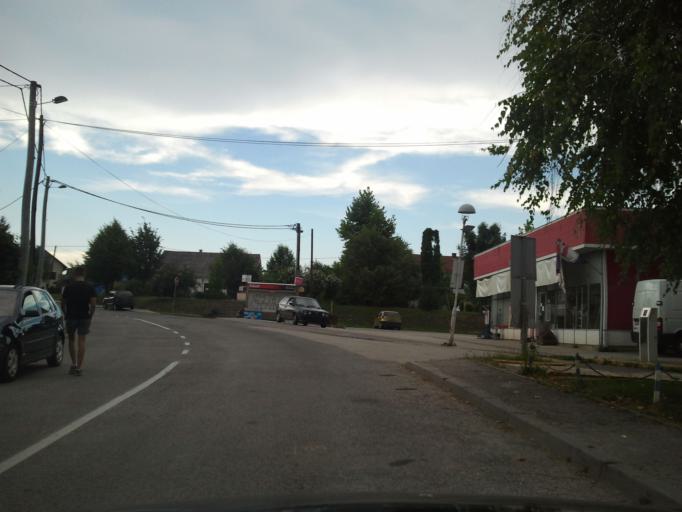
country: HR
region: Sisacko-Moslavacka
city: Gvozd
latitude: 45.4851
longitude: 15.9921
